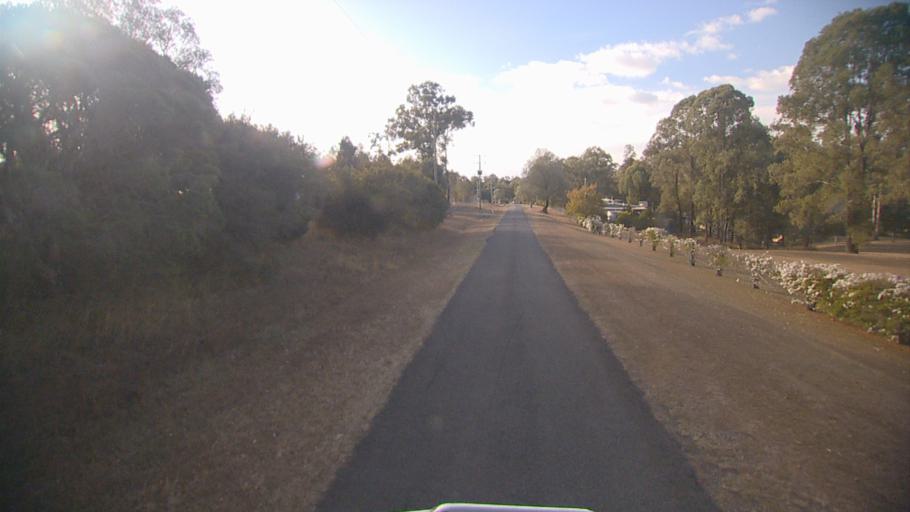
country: AU
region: Queensland
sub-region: Logan
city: Cedar Vale
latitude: -27.8812
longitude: 153.0208
